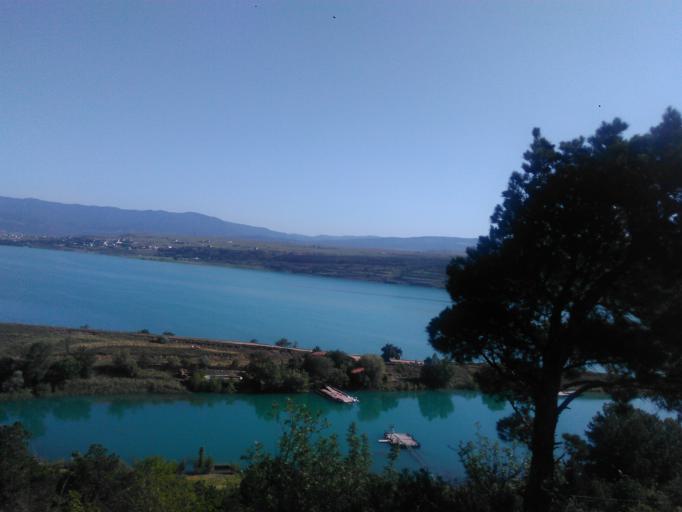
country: GE
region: T'bilisi
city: Tbilisi
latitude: 41.7391
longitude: 44.8422
